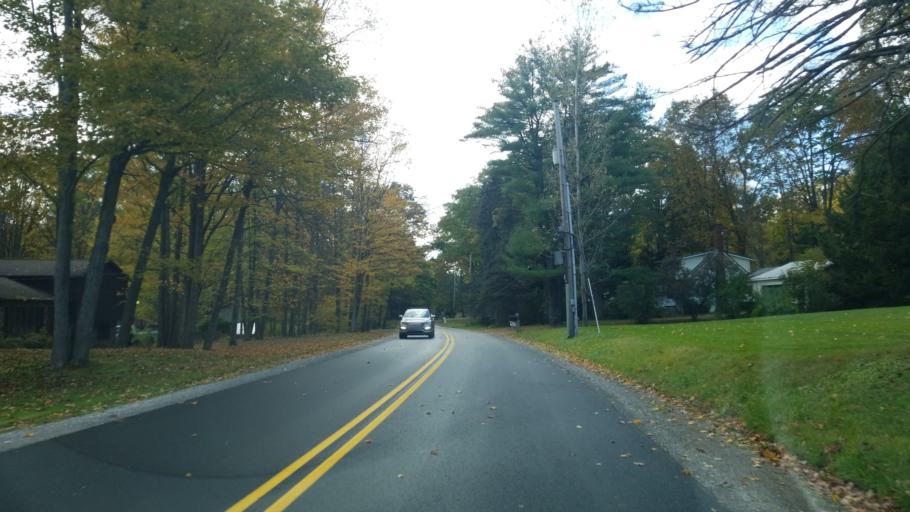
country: US
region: Pennsylvania
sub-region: Clearfield County
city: Sandy
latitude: 41.0898
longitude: -78.7925
